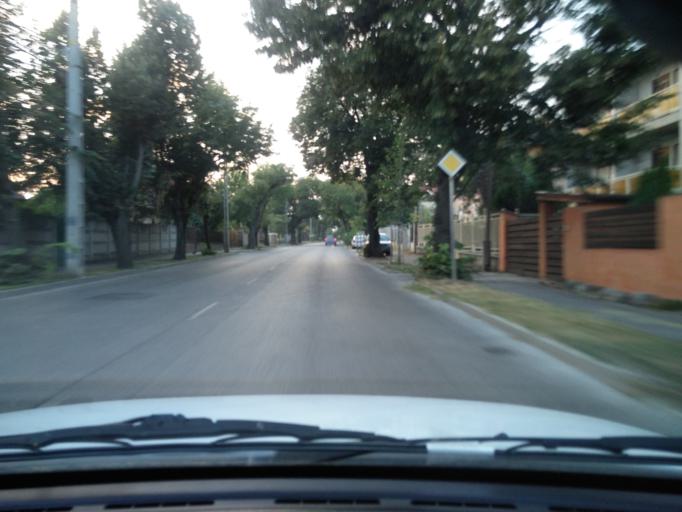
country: HU
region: Budapest
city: Budapest XXI. keruelet
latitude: 47.4116
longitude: 19.0878
